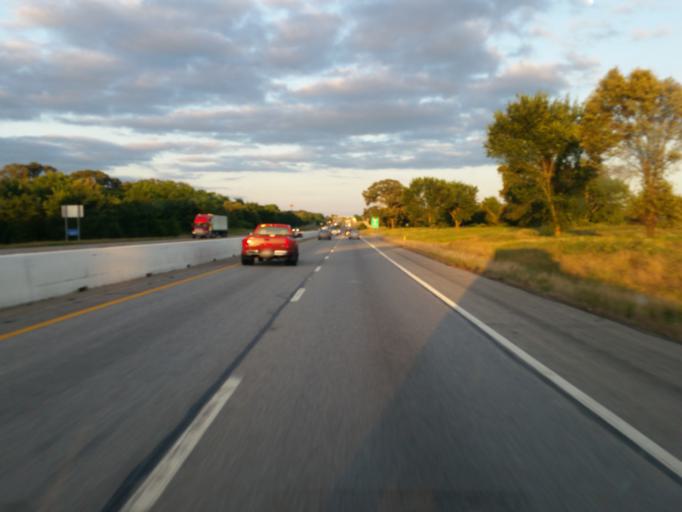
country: US
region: Texas
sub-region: Van Zandt County
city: Van
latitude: 32.5108
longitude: -95.6669
